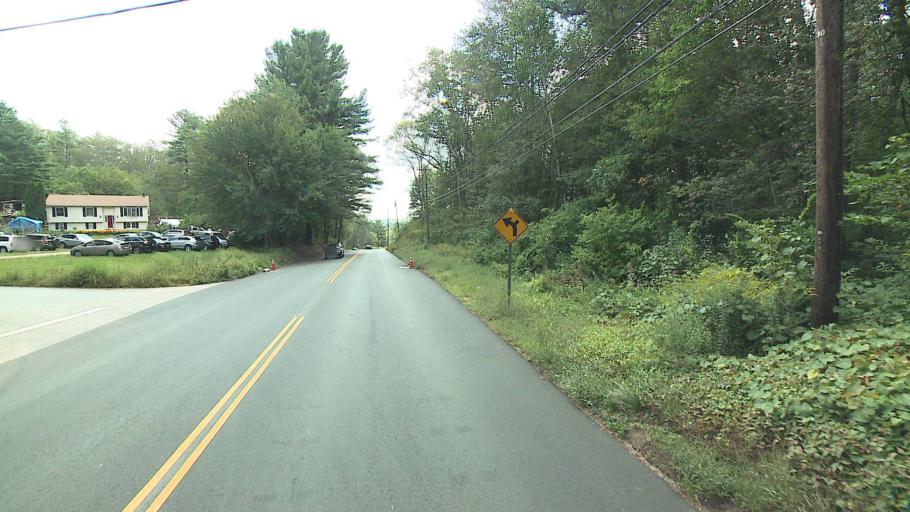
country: US
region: Connecticut
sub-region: Windham County
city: Thompson
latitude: 41.9210
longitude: -71.8404
